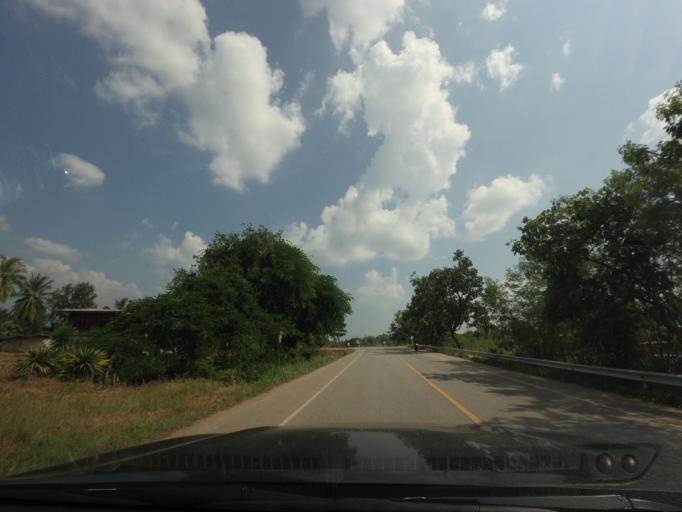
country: TH
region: Phitsanulok
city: Chat Trakan
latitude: 17.2605
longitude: 100.5566
